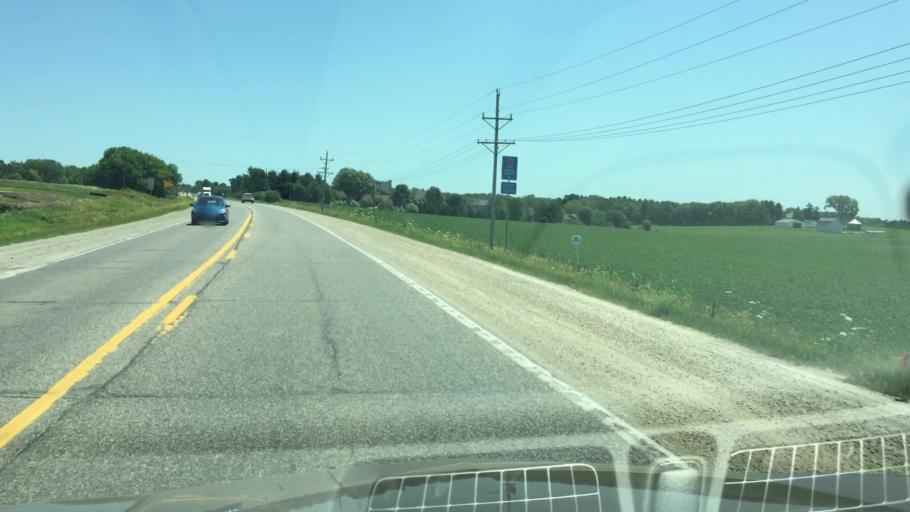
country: US
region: Iowa
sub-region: Linn County
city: Mount Vernon
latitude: 41.9160
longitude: -91.4206
